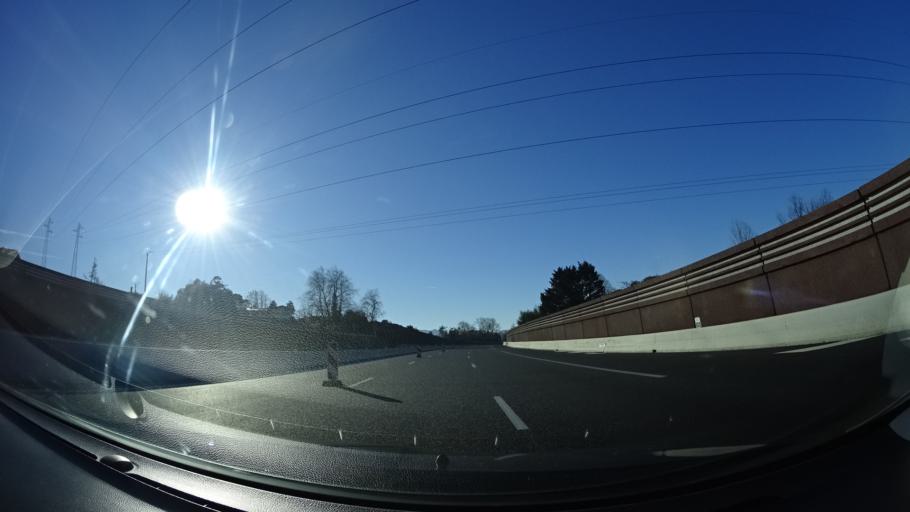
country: FR
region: Aquitaine
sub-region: Departement des Pyrenees-Atlantiques
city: Saint-Jean-de-Luz
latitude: 43.3950
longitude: -1.6356
